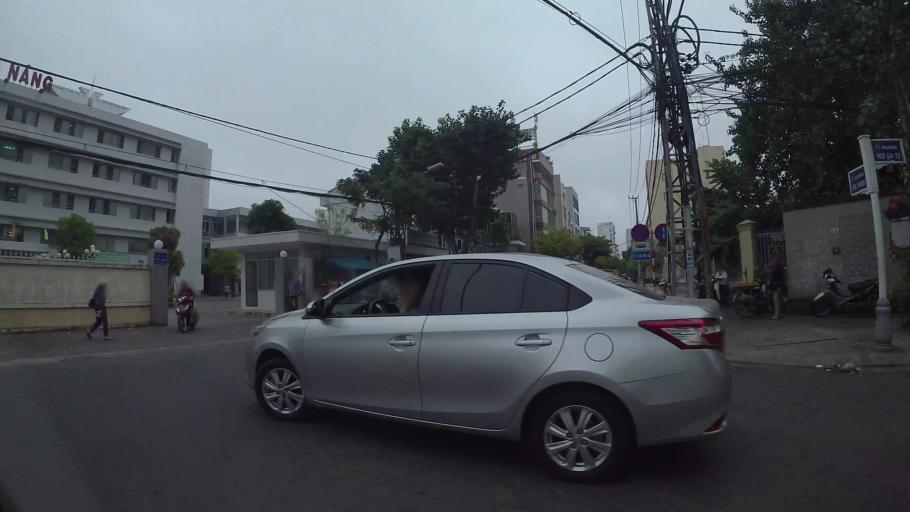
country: VN
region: Da Nang
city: Da Nang
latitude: 16.0721
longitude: 108.2165
